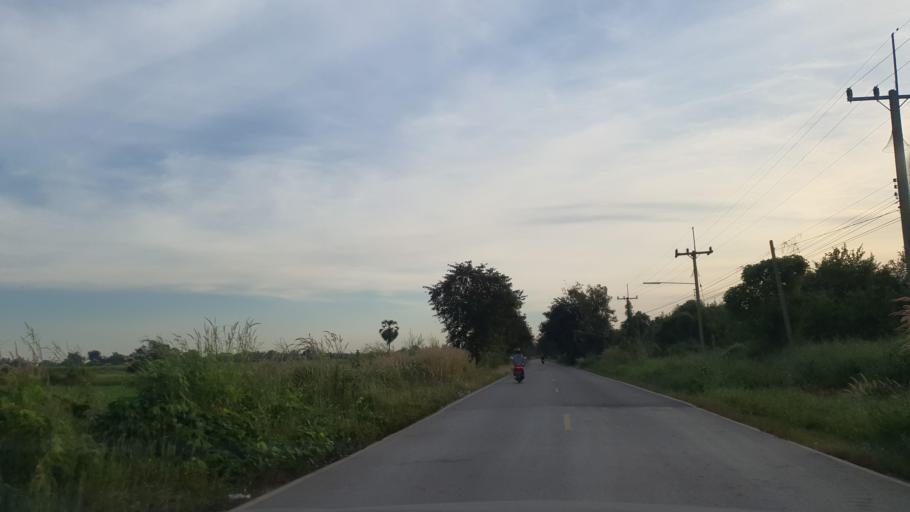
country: TH
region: Nakhon Sawan
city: Nakhon Sawan
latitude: 15.6613
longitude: 100.0490
